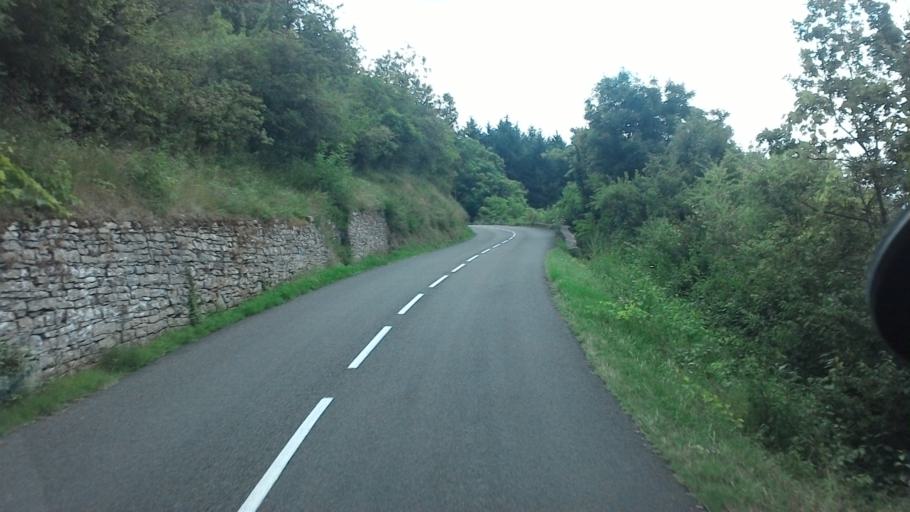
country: FR
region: Rhone-Alpes
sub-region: Departement de l'Ain
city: Saint-Sorlin-en-Bugey
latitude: 45.8921
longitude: 5.3648
